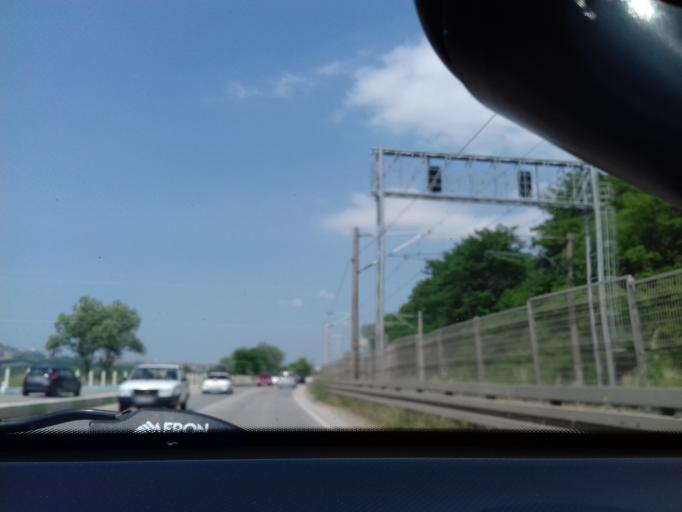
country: TR
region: Sakarya
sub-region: Merkez
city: Sapanca
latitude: 40.7095
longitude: 30.3203
